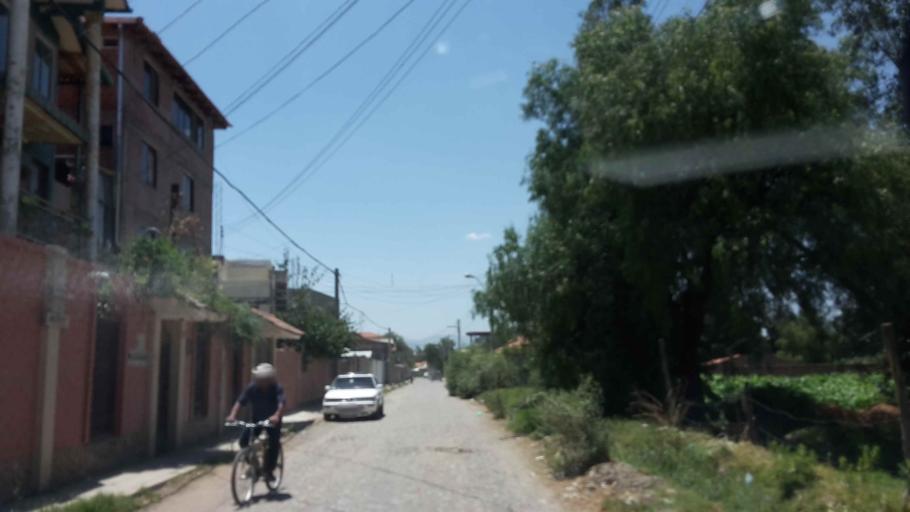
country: BO
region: Cochabamba
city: Cochabamba
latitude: -17.3651
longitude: -66.1976
